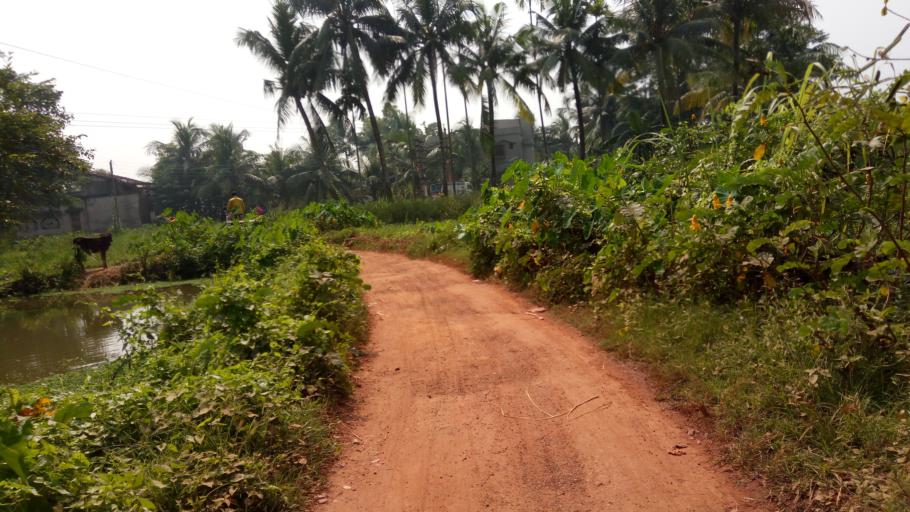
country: IN
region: West Bengal
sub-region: Purba Medinipur
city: Mahishadal
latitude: 22.1717
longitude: 87.9116
